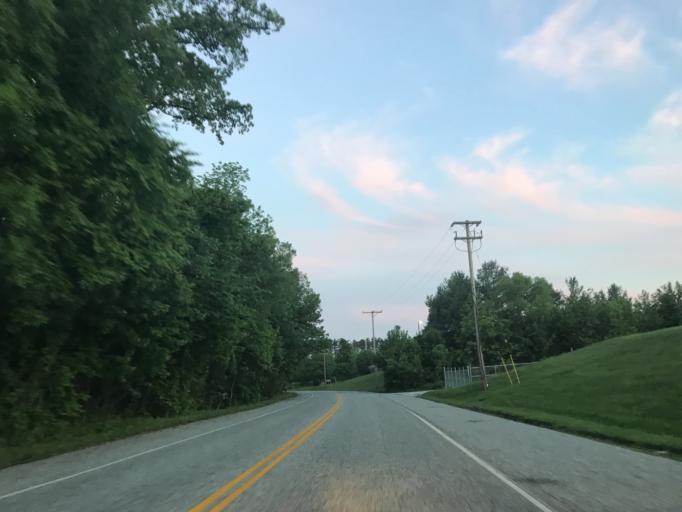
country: US
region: Maryland
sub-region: Harford County
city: Joppatowne
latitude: 39.4467
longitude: -76.3205
